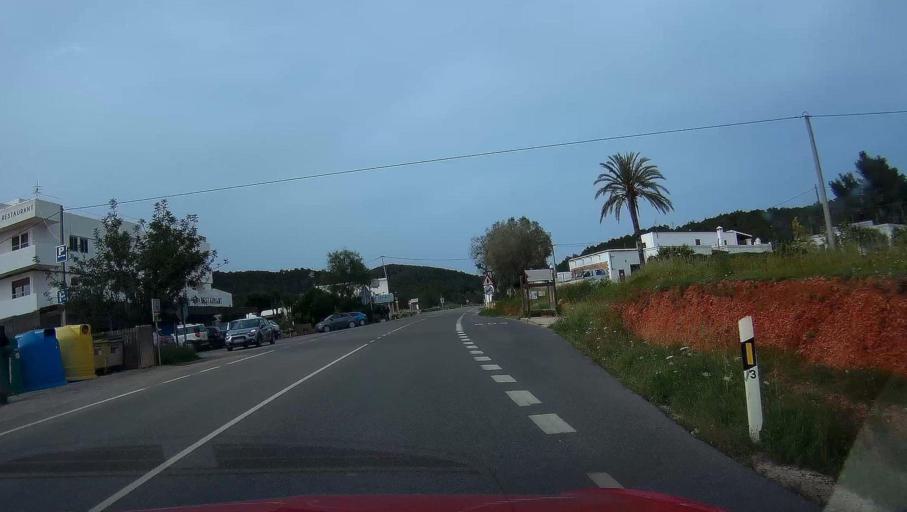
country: ES
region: Balearic Islands
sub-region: Illes Balears
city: Sant Joan de Labritja
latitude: 39.0665
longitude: 1.4944
